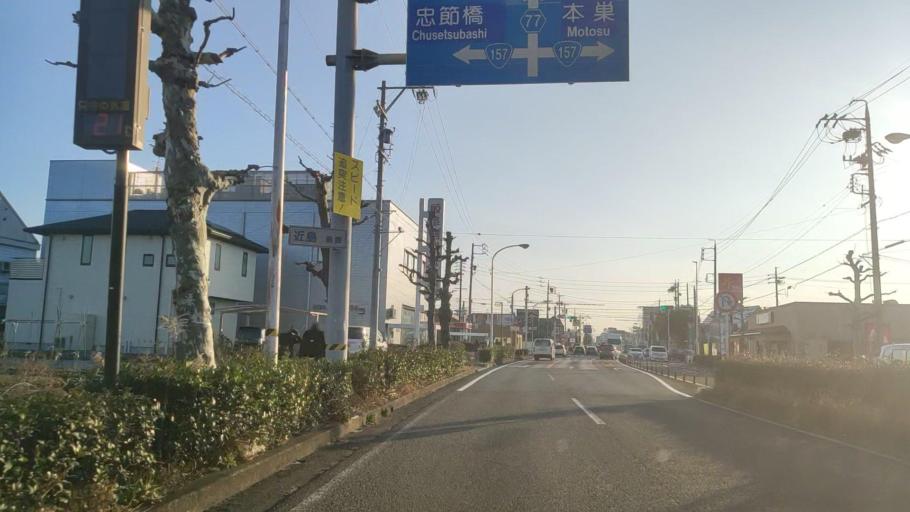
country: JP
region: Gifu
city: Gifu-shi
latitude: 35.4319
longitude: 136.7350
